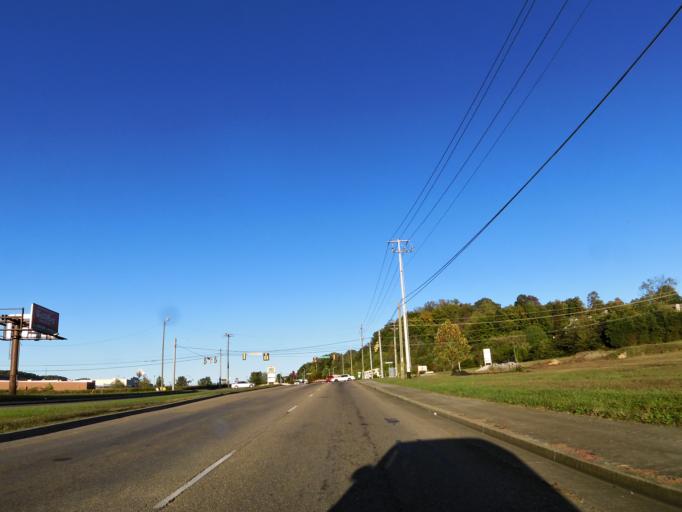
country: US
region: Tennessee
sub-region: Knox County
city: Knoxville
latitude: 36.0018
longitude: -84.0250
